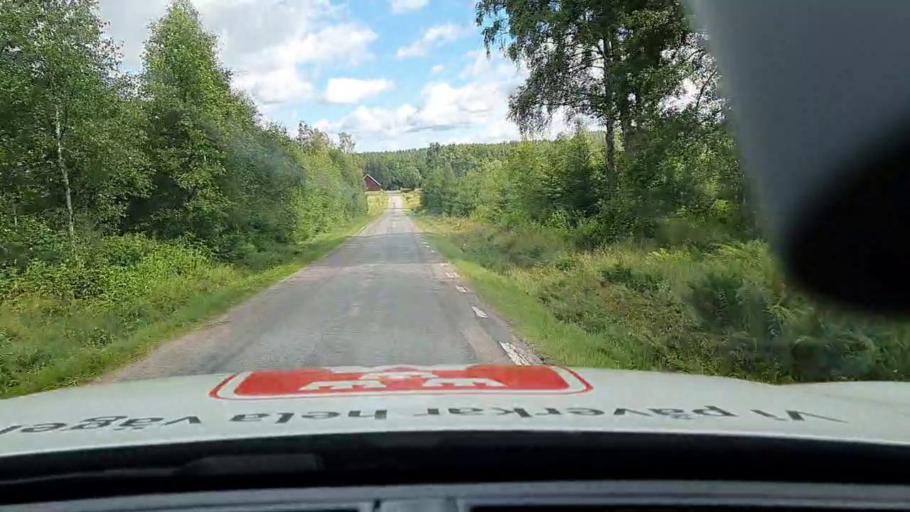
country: SE
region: Vaestra Goetaland
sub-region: Karlsborgs Kommun
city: Molltorp
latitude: 58.6042
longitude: 14.3036
